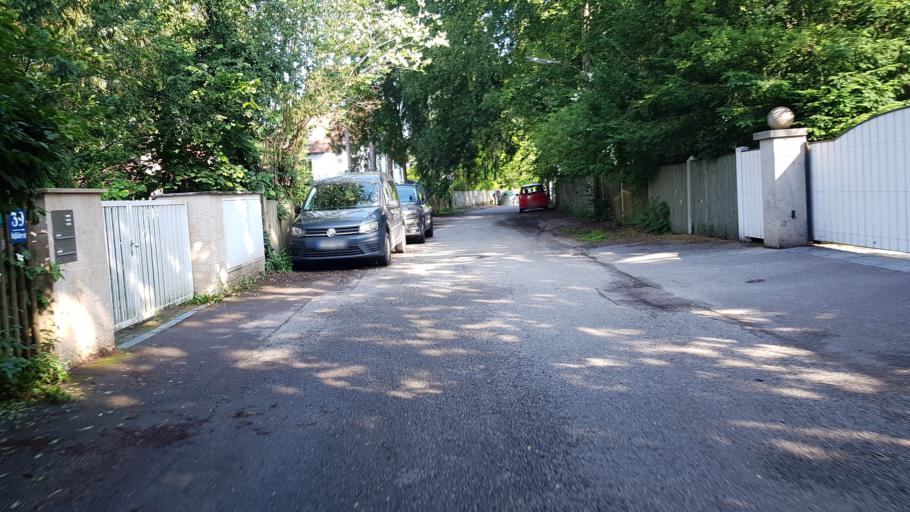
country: DE
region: Bavaria
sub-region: Upper Bavaria
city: Pasing
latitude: 48.1737
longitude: 11.4802
